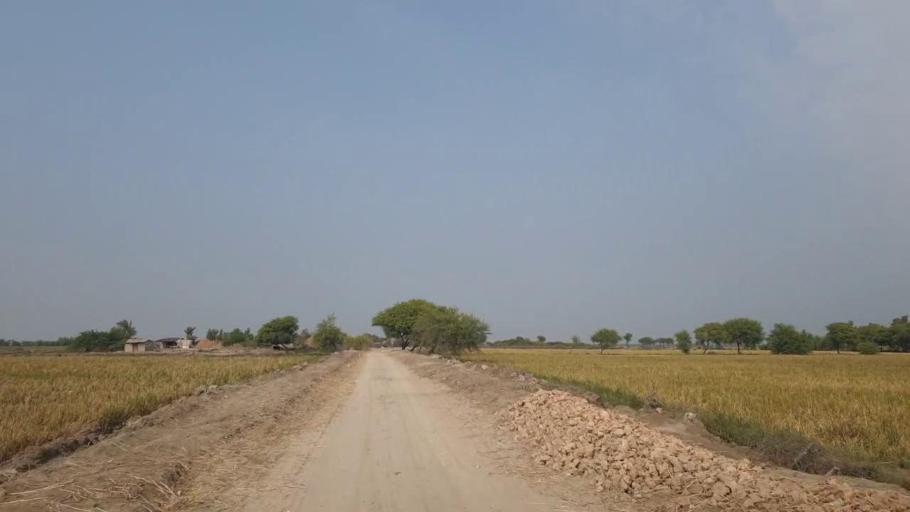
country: PK
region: Sindh
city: Badin
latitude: 24.6145
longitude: 68.7411
